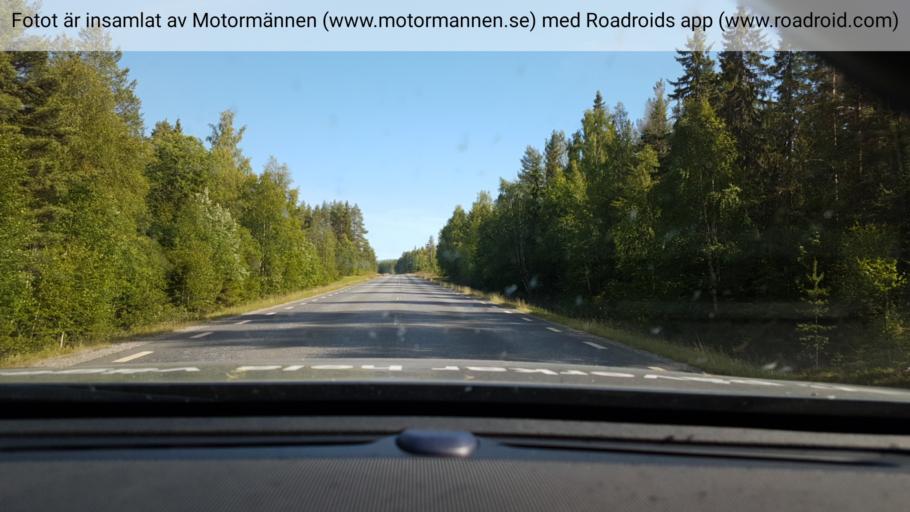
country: SE
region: Vaesterbotten
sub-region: Lycksele Kommun
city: Soderfors
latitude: 64.7827
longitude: 18.1211
